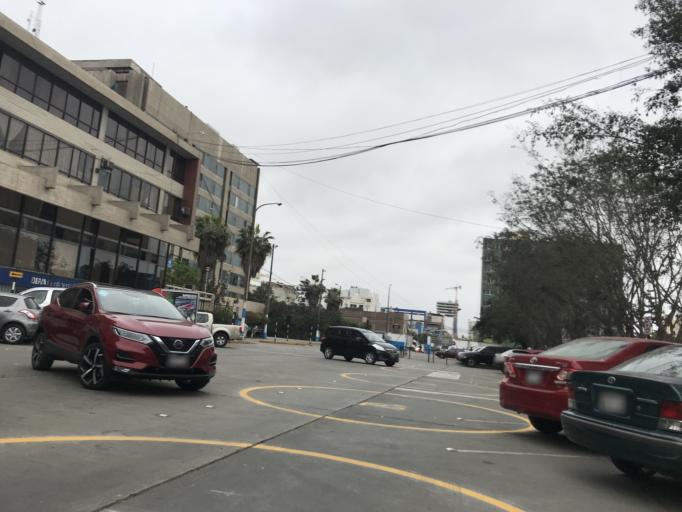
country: PE
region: Lima
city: Lima
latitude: -12.0788
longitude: -77.0379
